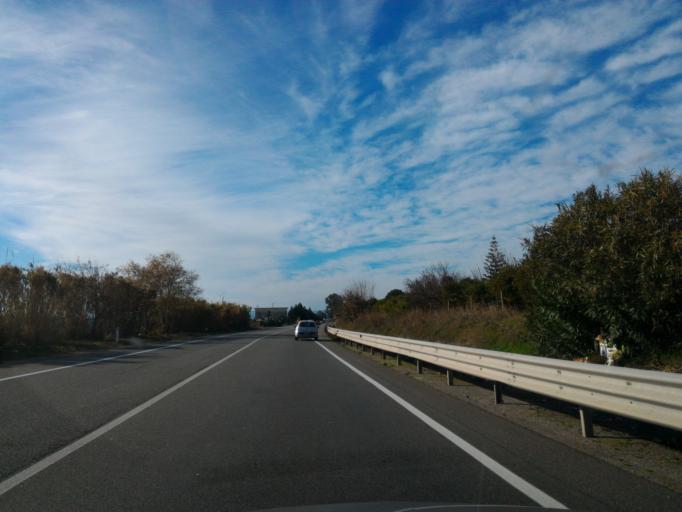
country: IT
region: Calabria
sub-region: Provincia di Catanzaro
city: Sellia Marina
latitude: 38.8745
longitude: 16.7006
